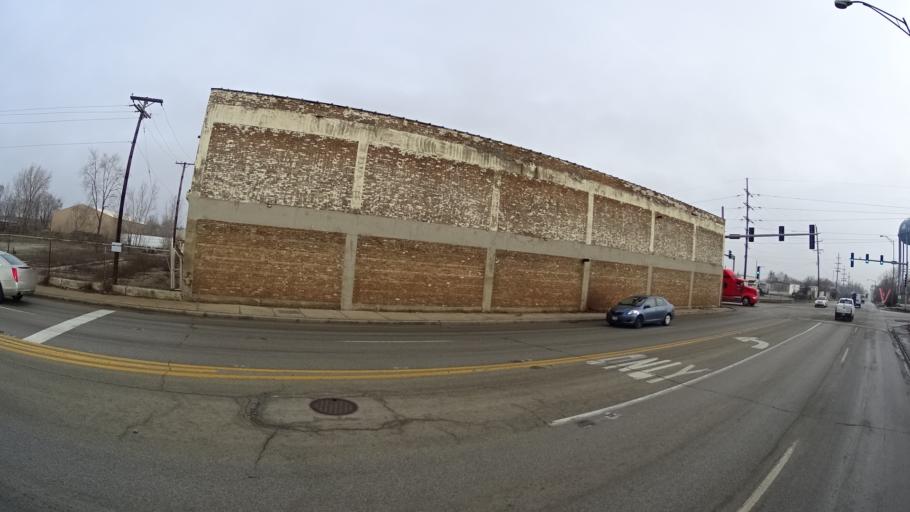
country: US
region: Illinois
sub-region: Cook County
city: Chicago Heights
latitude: 41.5061
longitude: -87.6168
